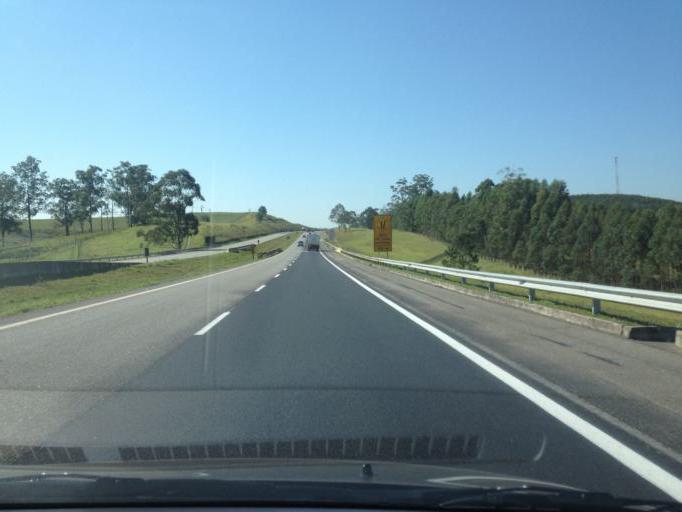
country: BR
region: Sao Paulo
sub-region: Guararema
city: Guararema
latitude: -23.3591
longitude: -46.1212
